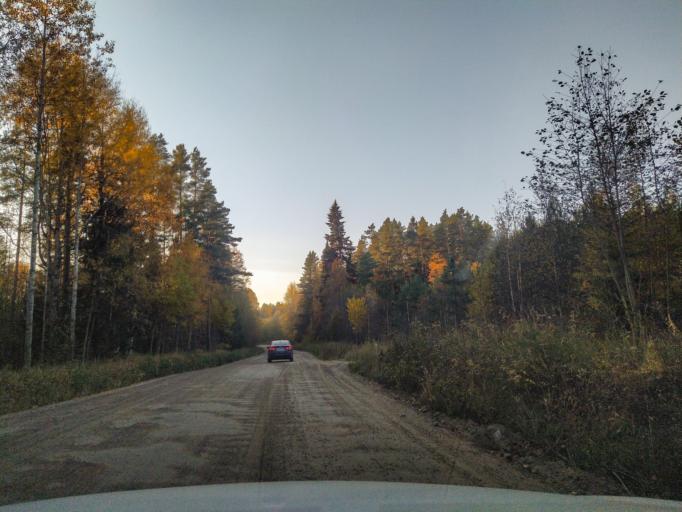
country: RU
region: Leningrad
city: Kuznechnoye
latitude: 61.3297
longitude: 29.9778
